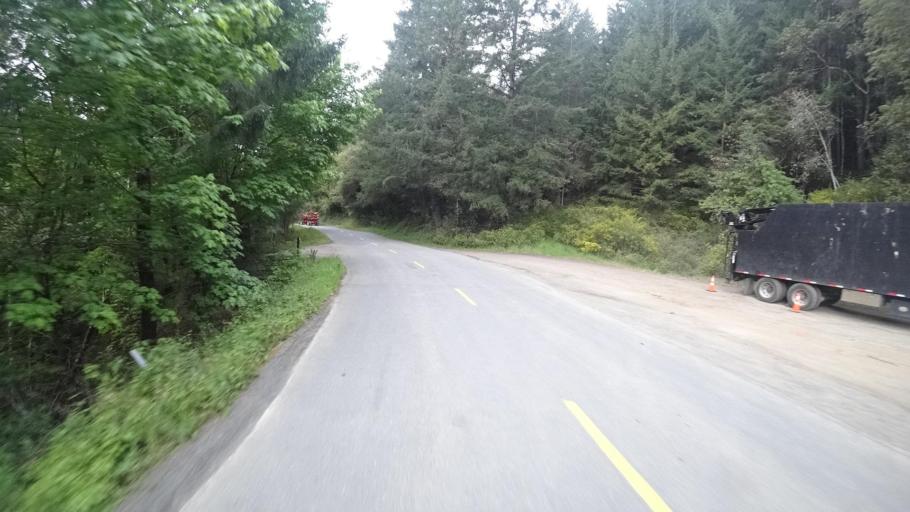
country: US
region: California
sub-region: Humboldt County
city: Redway
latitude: 40.2957
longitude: -123.8317
